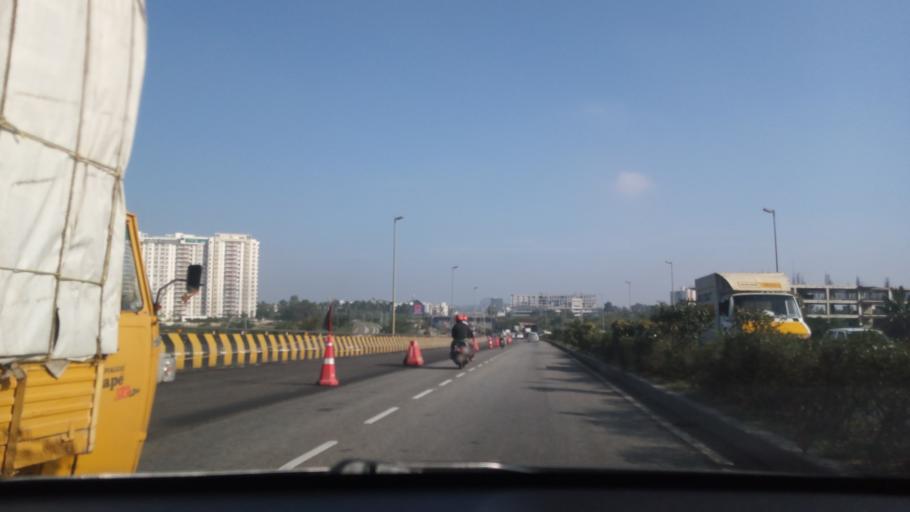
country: IN
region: Karnataka
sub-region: Bangalore Urban
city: Yelahanka
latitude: 13.0889
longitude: 77.5963
